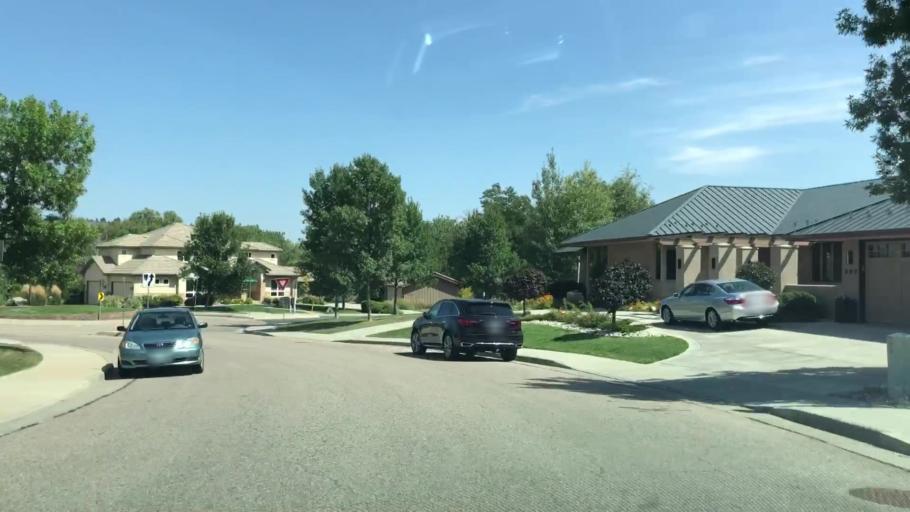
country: US
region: Colorado
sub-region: Larimer County
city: Loveland
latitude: 40.4011
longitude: -105.1523
